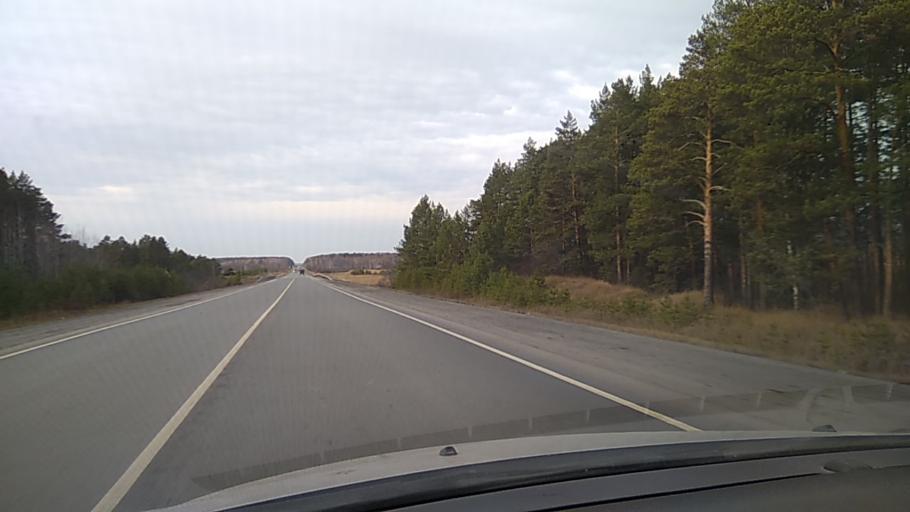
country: RU
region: Sverdlovsk
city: Troitskiy
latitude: 57.0890
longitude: 63.8683
